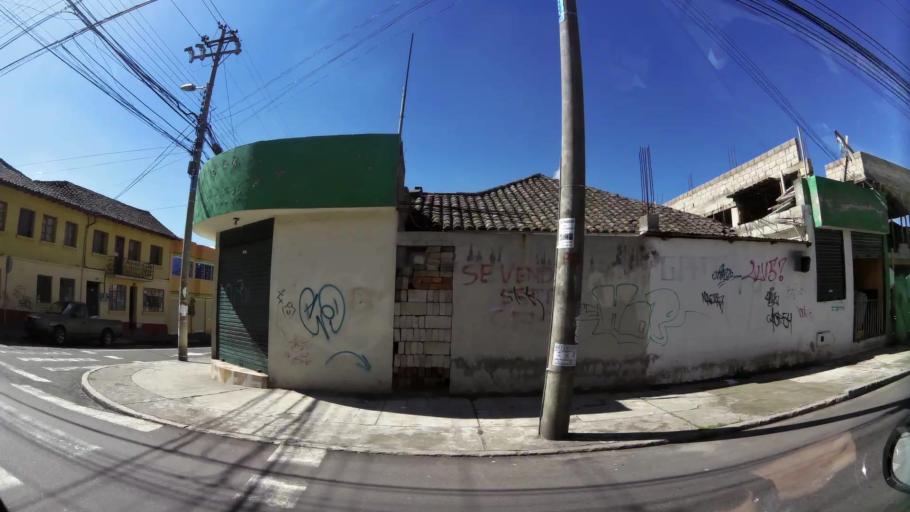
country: EC
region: Pichincha
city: Quito
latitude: -0.2437
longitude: -78.5274
